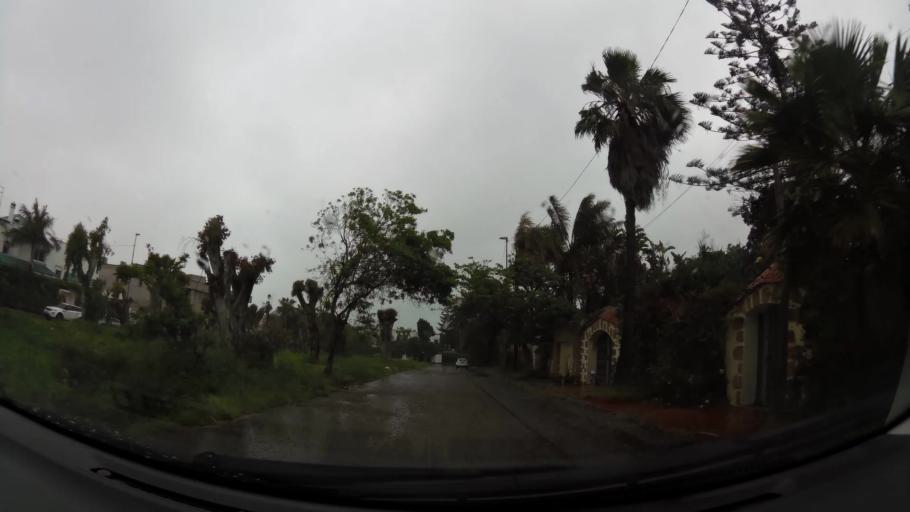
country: MA
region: Grand Casablanca
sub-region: Casablanca
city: Casablanca
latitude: 33.5895
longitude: -7.6710
